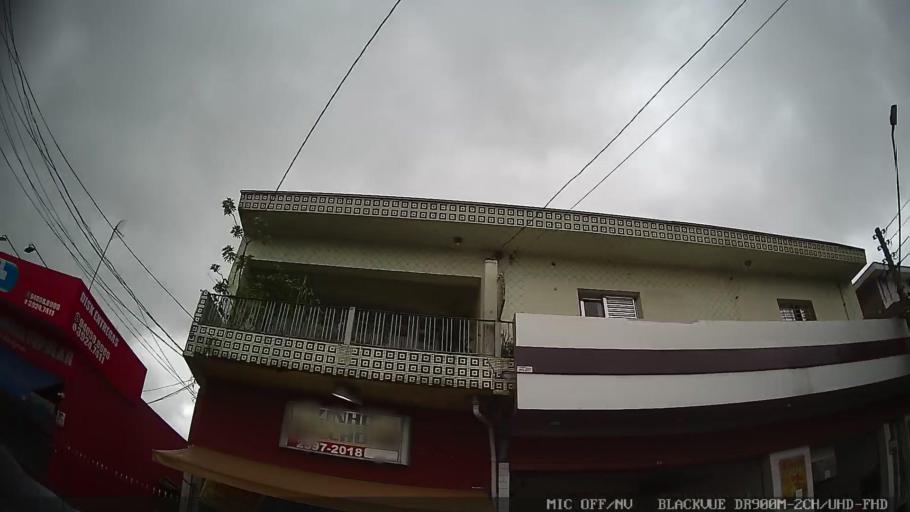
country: BR
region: Sao Paulo
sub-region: Osasco
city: Osasco
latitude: -23.4804
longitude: -46.7130
